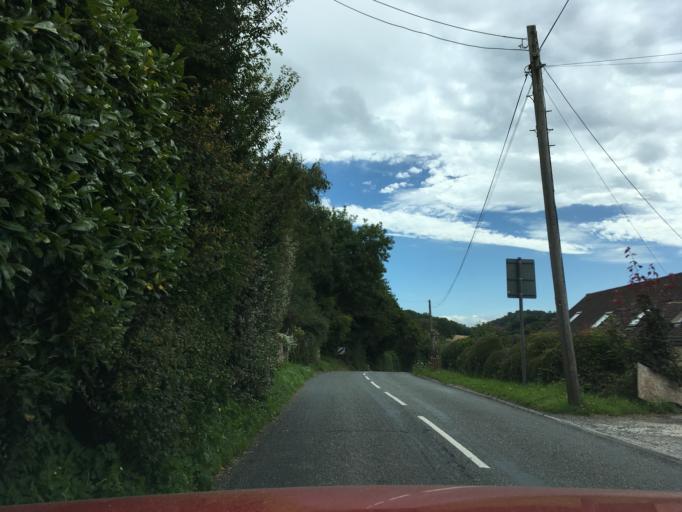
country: GB
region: England
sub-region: North Somerset
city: Churchill
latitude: 51.3086
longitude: -2.7987
